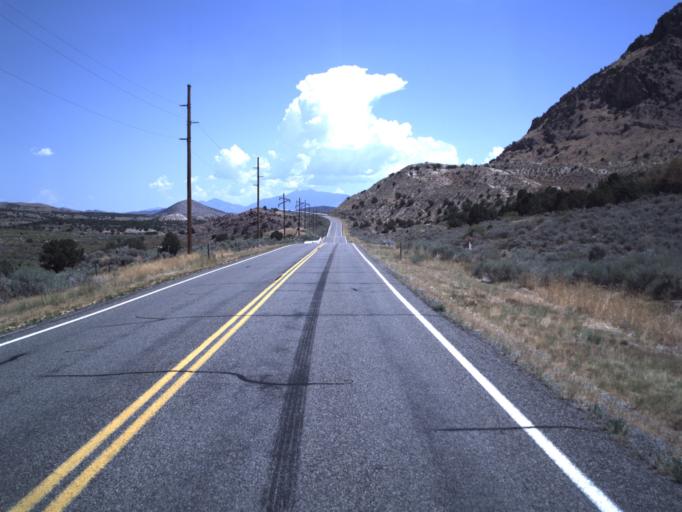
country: US
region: Utah
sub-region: Millard County
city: Delta
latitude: 39.5491
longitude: -112.2265
